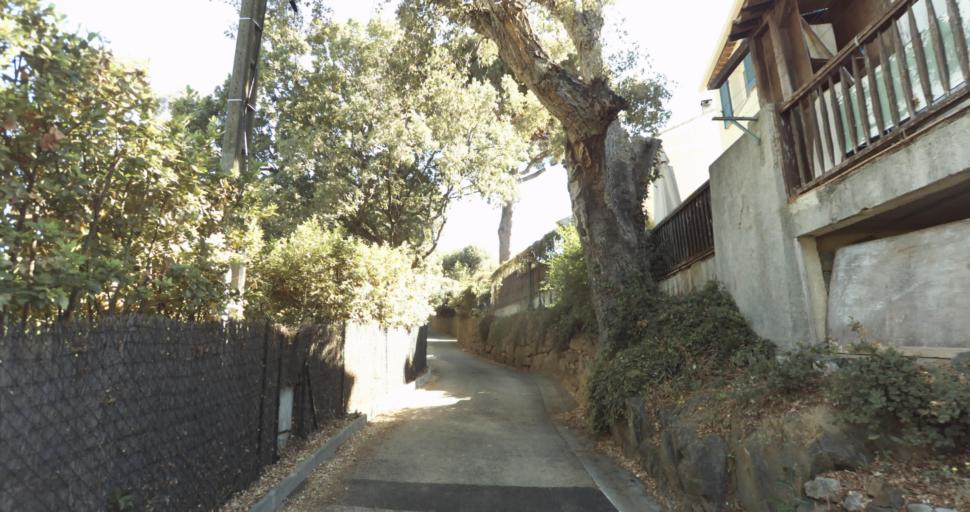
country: FR
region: Provence-Alpes-Cote d'Azur
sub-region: Departement du Var
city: Gassin
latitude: 43.2261
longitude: 6.5853
